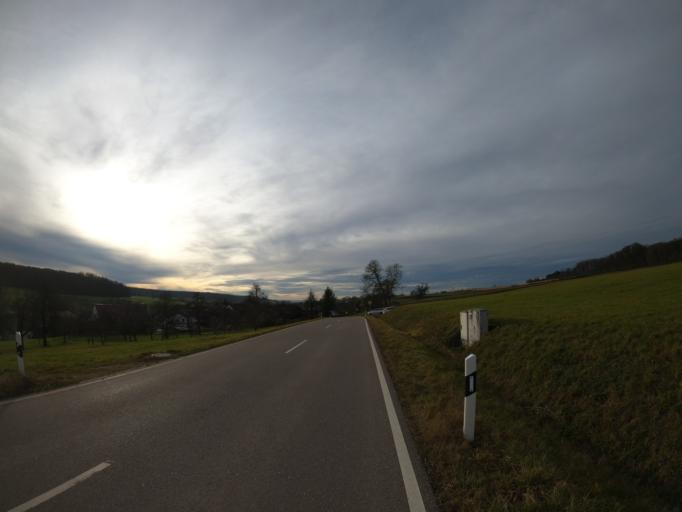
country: DE
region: Baden-Wuerttemberg
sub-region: Regierungsbezirk Stuttgart
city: Waschenbeuren
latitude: 48.7322
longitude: 9.6857
